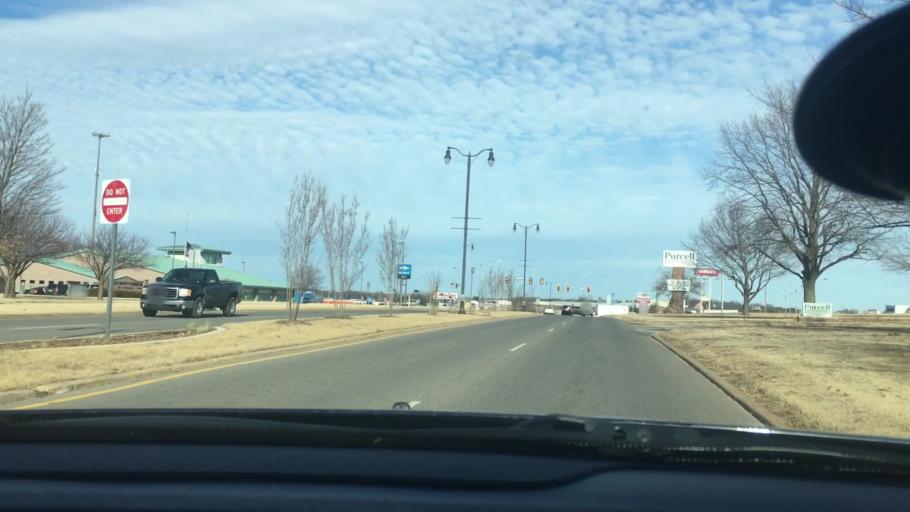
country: US
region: Oklahoma
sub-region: McClain County
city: Purcell
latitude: 35.0280
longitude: -97.3657
